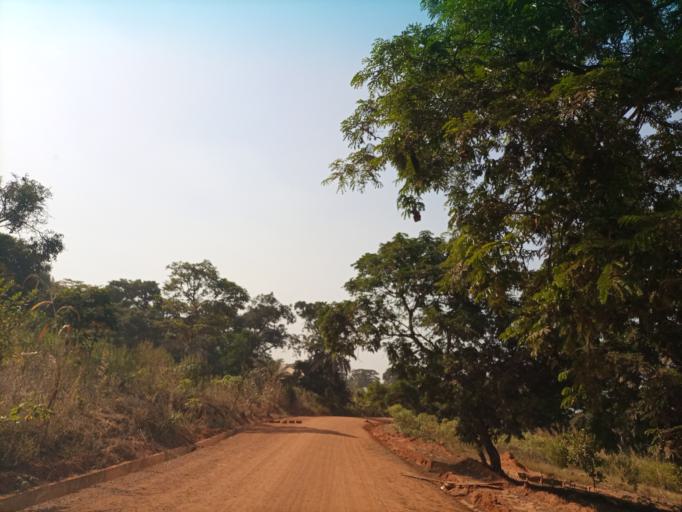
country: NG
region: Enugu
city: Aku
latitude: 6.7046
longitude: 7.3135
